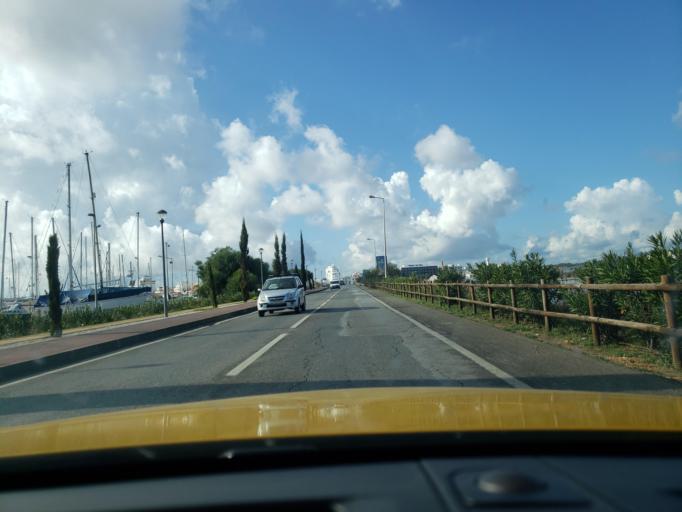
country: PT
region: Faro
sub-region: Portimao
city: Portimao
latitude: 37.1377
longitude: -8.5269
